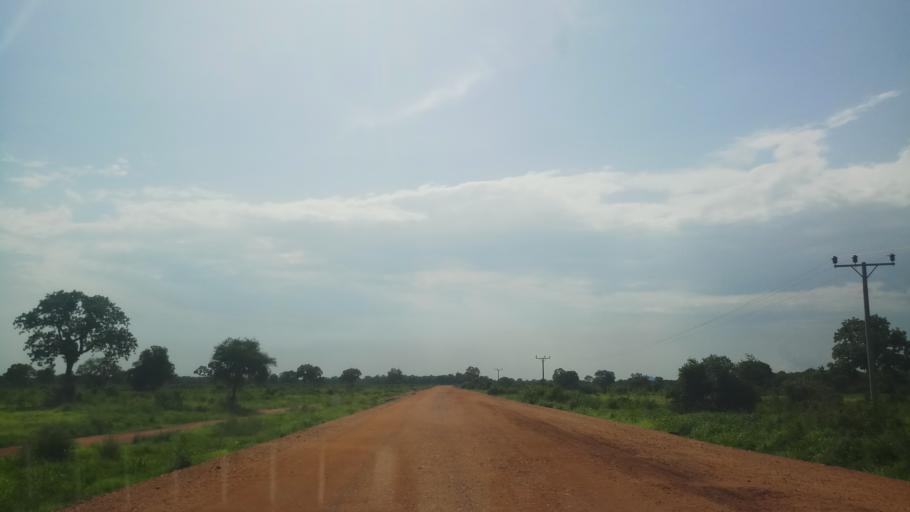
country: ET
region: Gambela
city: Gambela
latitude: 8.1320
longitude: 34.3837
